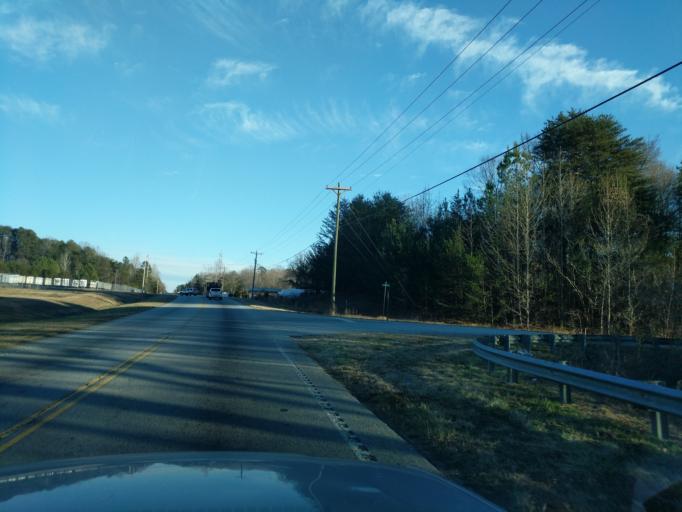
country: US
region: South Carolina
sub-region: Anderson County
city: Williamston
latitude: 34.6419
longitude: -82.4490
